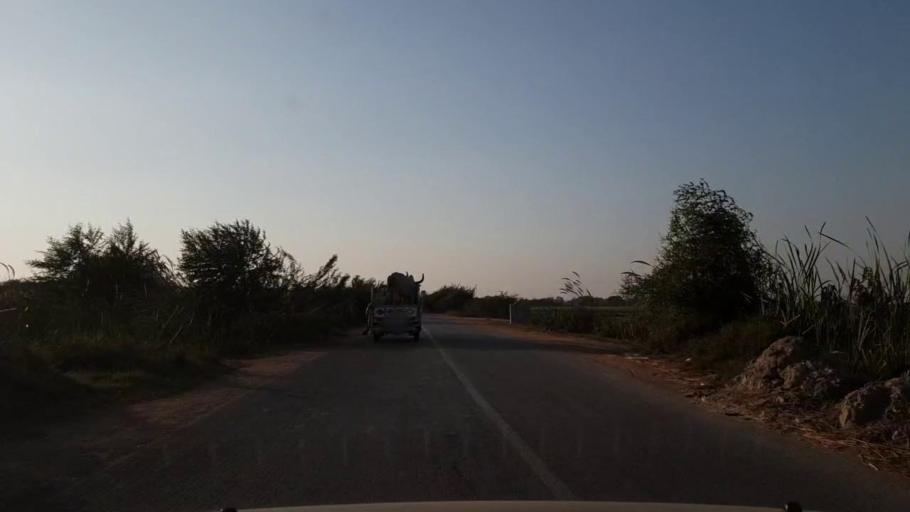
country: PK
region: Sindh
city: Mirpur Batoro
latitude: 24.6896
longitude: 68.1799
